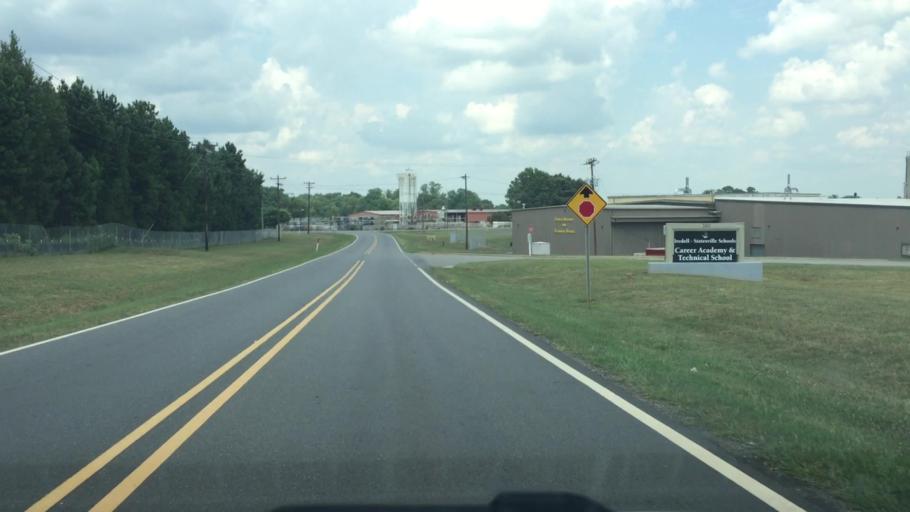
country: US
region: North Carolina
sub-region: Iredell County
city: Troutman
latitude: 35.7153
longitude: -80.8885
